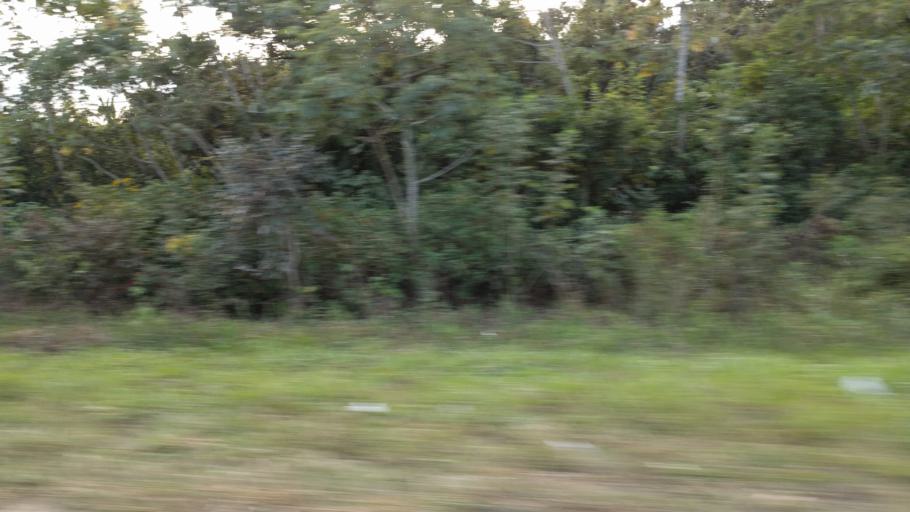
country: BO
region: Santa Cruz
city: Buena Vista
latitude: -17.4380
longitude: -63.6417
